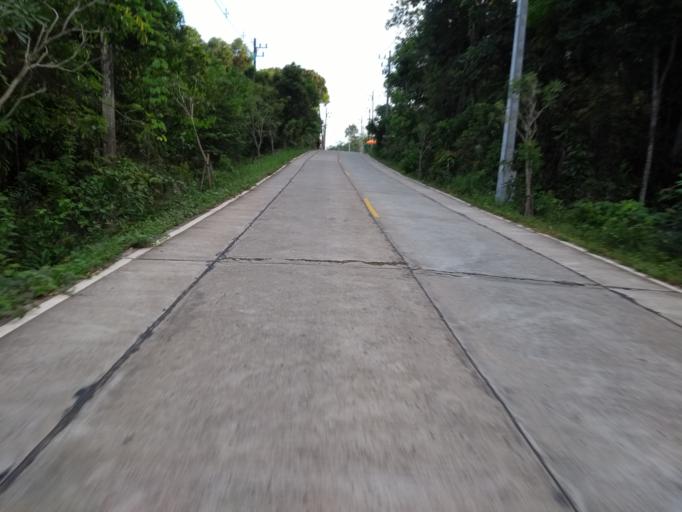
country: TH
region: Trat
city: Ko Kut
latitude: 11.6271
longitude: 102.5466
